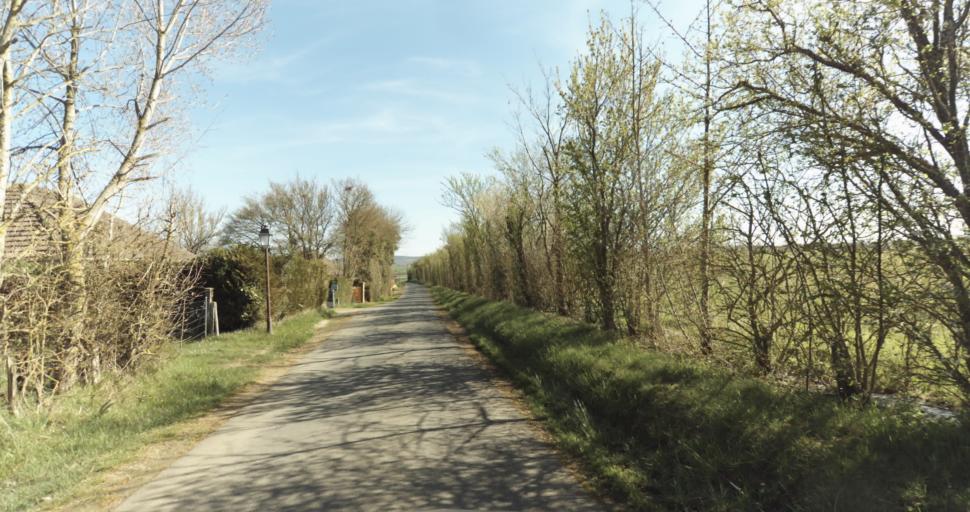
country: FR
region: Lower Normandy
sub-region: Departement du Calvados
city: Saint-Pierre-sur-Dives
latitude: 49.0503
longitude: -0.0197
